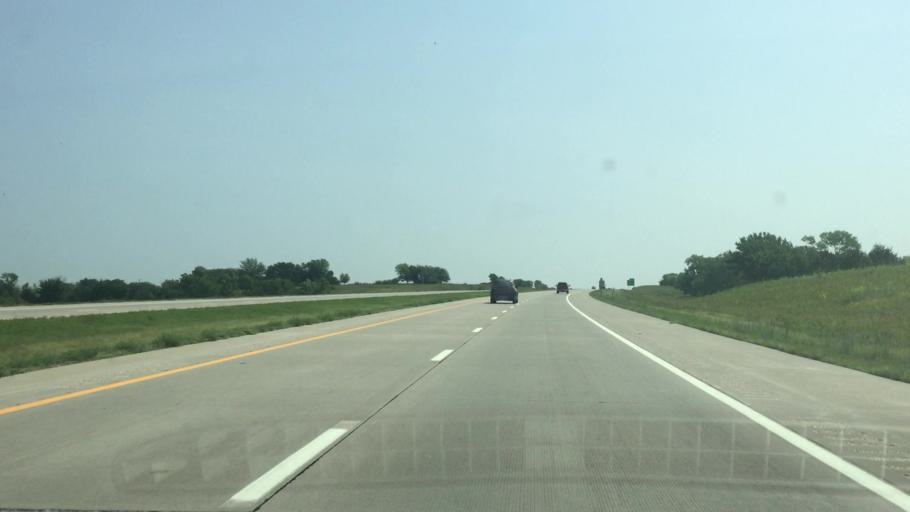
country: US
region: Kansas
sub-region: Osage County
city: Lyndon
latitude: 38.4435
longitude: -95.6673
